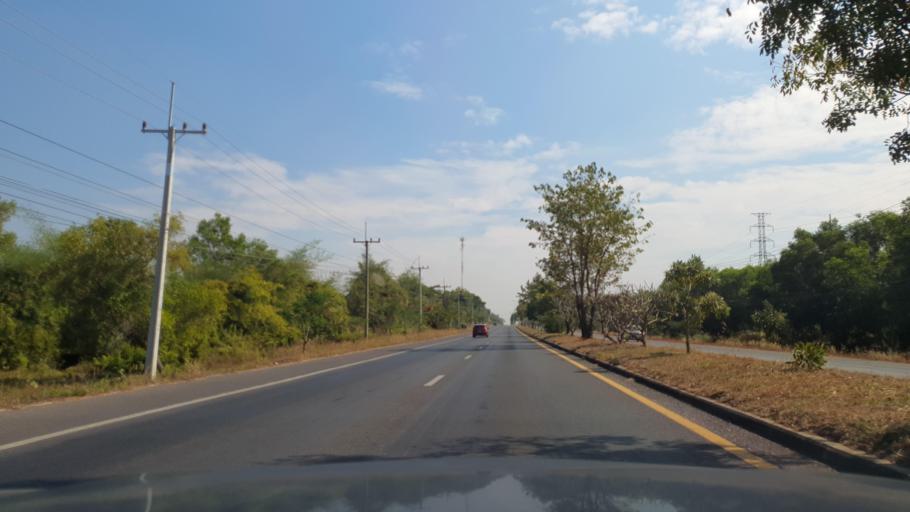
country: TH
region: Maha Sarakham
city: Kantharawichai
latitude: 16.3898
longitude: 103.2679
